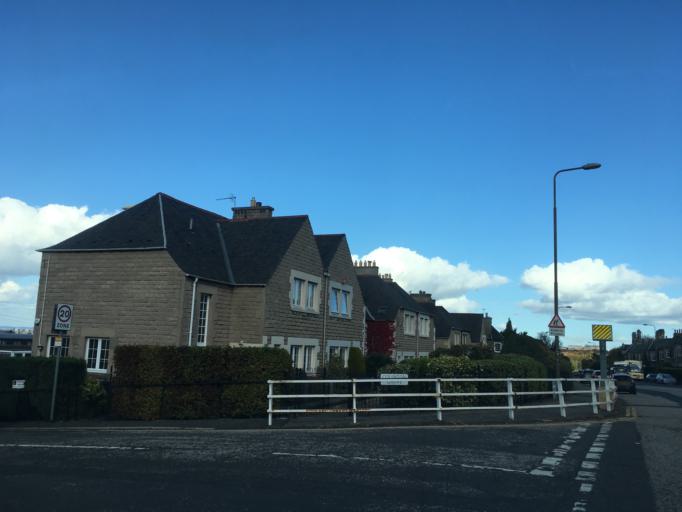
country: GB
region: Scotland
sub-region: Edinburgh
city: Colinton
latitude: 55.9247
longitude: -3.2353
